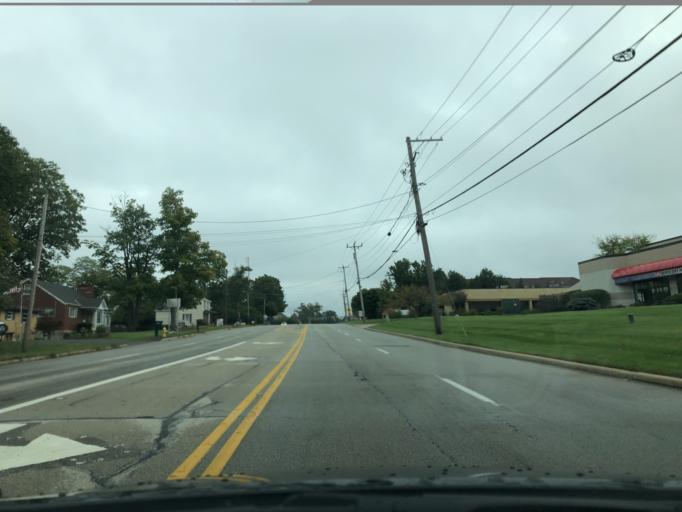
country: US
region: Ohio
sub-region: Hamilton County
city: Highpoint
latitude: 39.2812
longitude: -84.3605
